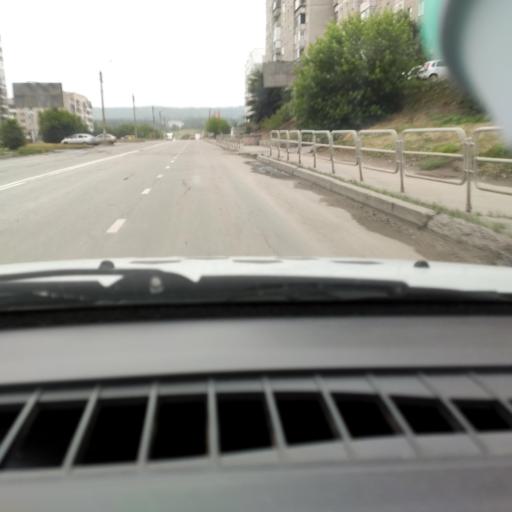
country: RU
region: Chelyabinsk
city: Miass
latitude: 55.0455
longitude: 60.0976
